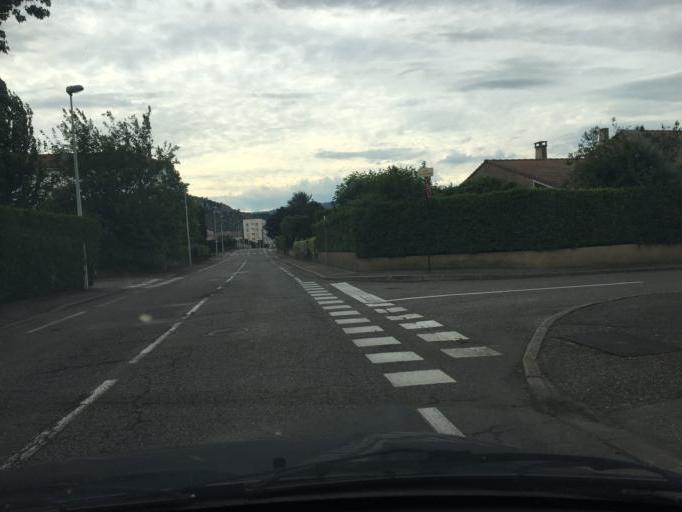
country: FR
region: Rhone-Alpes
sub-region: Departement de l'Ardeche
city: Guilherand-Granges
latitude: 44.9390
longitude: 4.8754
